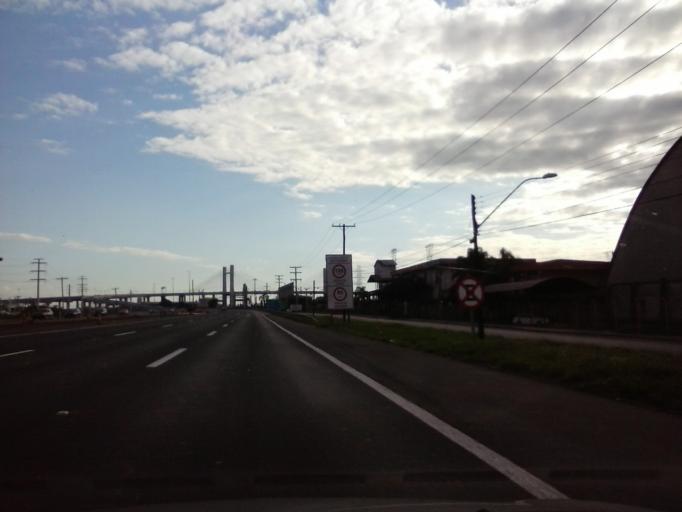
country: BR
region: Rio Grande do Sul
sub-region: Canoas
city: Canoas
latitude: -29.9708
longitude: -51.1903
